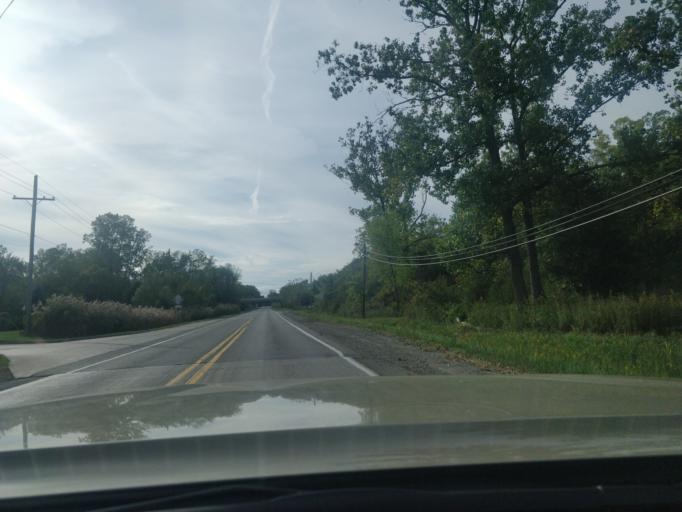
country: US
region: Michigan
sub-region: Wayne County
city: Romulus
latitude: 42.2088
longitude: -83.3874
